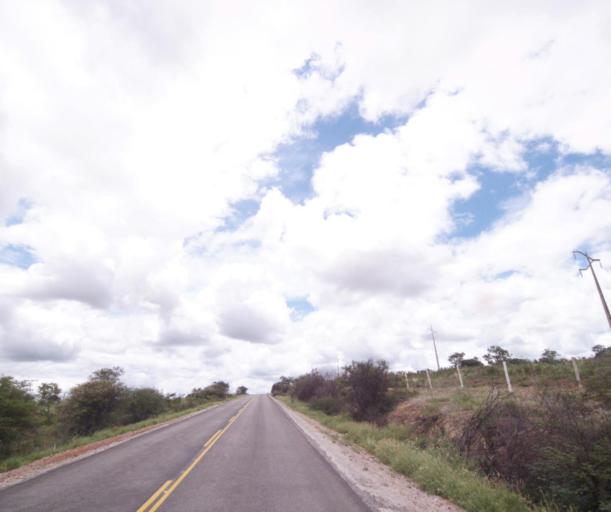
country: BR
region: Bahia
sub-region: Brumado
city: Brumado
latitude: -14.1533
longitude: -41.5128
